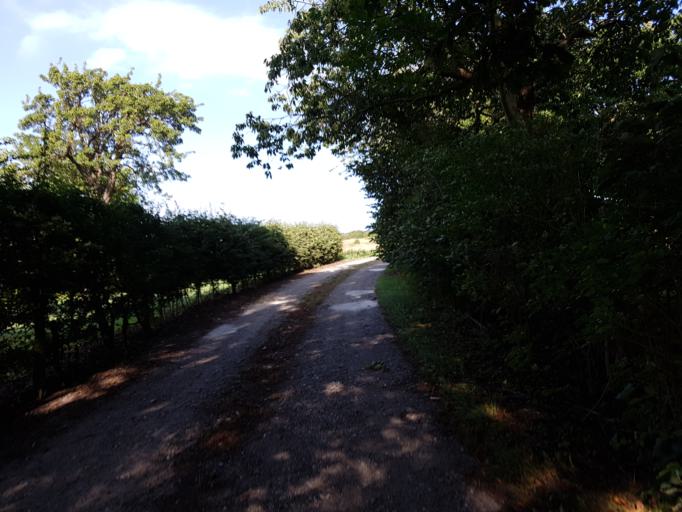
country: DK
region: Zealand
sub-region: Guldborgsund Kommune
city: Nykobing Falster
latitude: 54.6002
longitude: 11.9219
